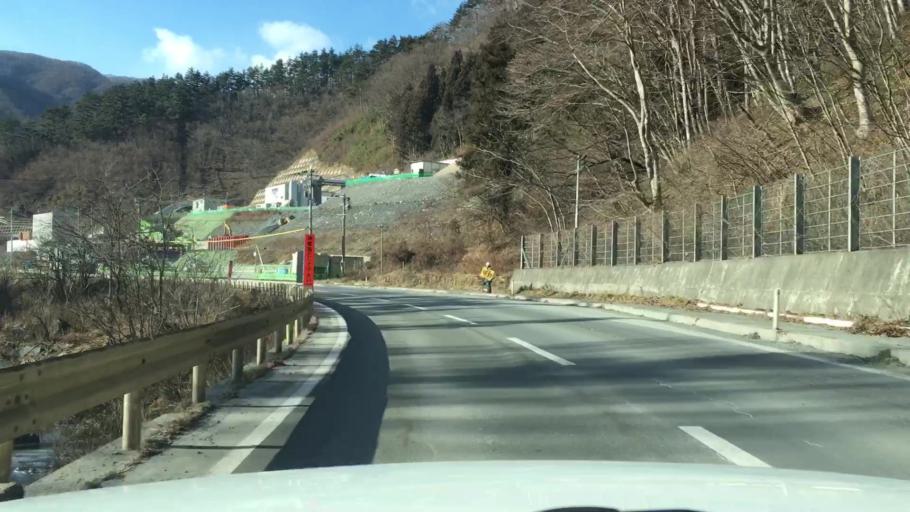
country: JP
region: Iwate
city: Miyako
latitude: 39.5963
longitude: 141.6582
